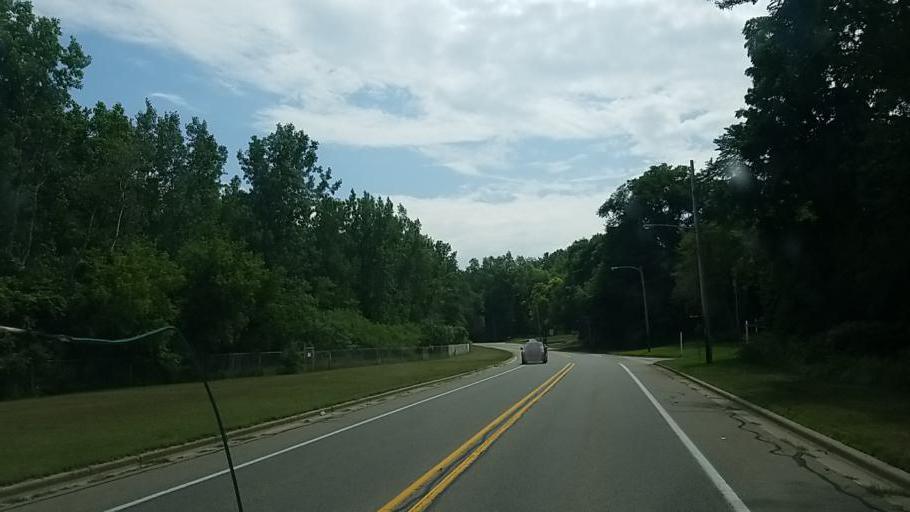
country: US
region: Michigan
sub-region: Kent County
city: Walker
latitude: 42.9994
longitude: -85.7184
